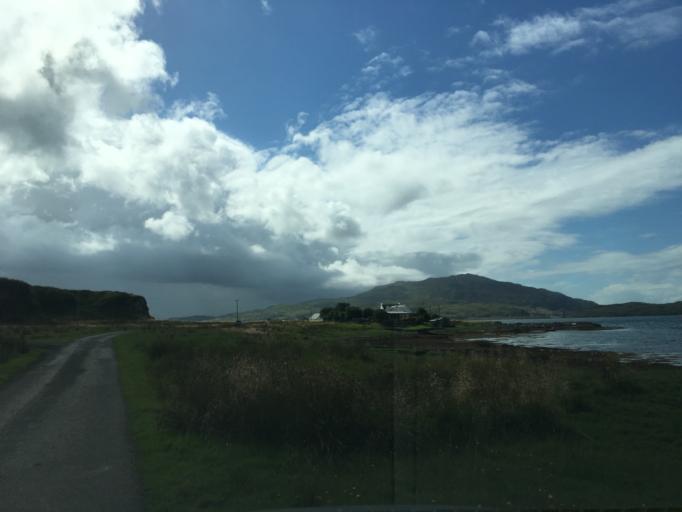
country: GB
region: Scotland
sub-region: Argyll and Bute
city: Isle Of Mull
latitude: 56.2159
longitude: -5.6554
